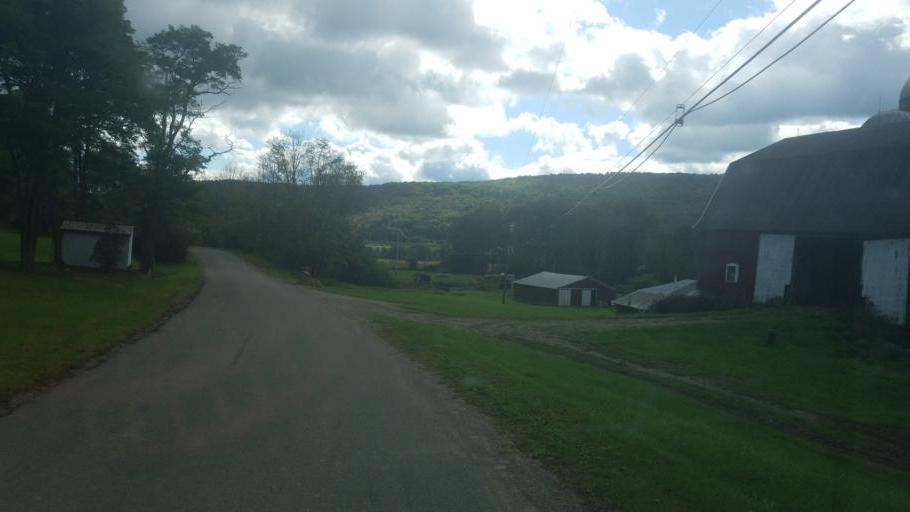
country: US
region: New York
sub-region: Allegany County
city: Cuba
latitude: 42.2180
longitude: -78.3292
